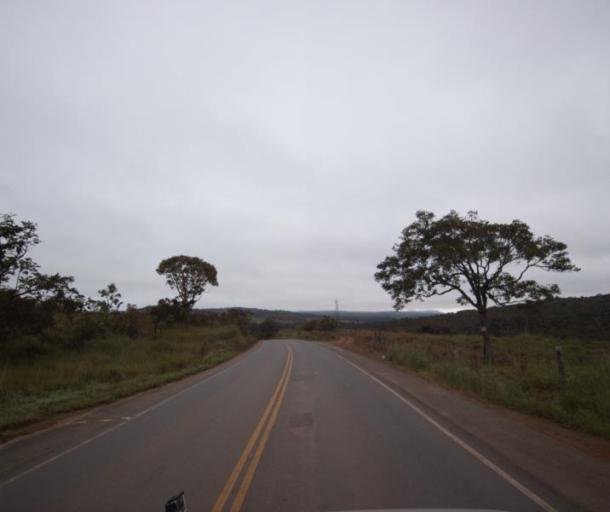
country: BR
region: Goias
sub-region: Pirenopolis
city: Pirenopolis
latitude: -15.8947
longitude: -48.7959
